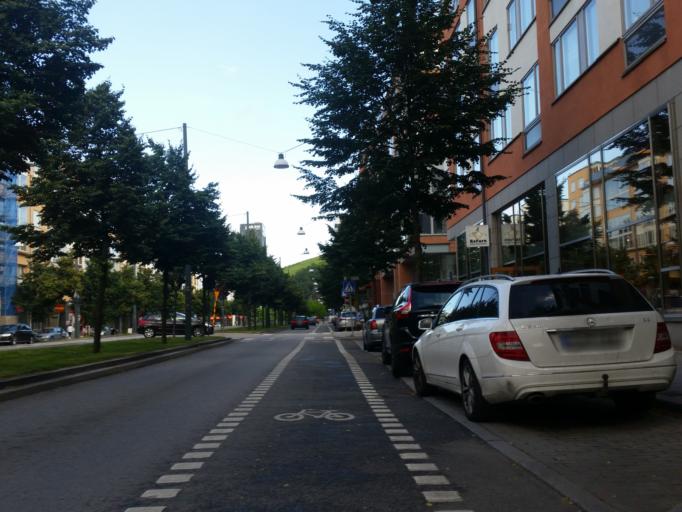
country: SE
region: Stockholm
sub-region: Stockholms Kommun
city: OEstermalm
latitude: 59.3032
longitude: 18.0993
